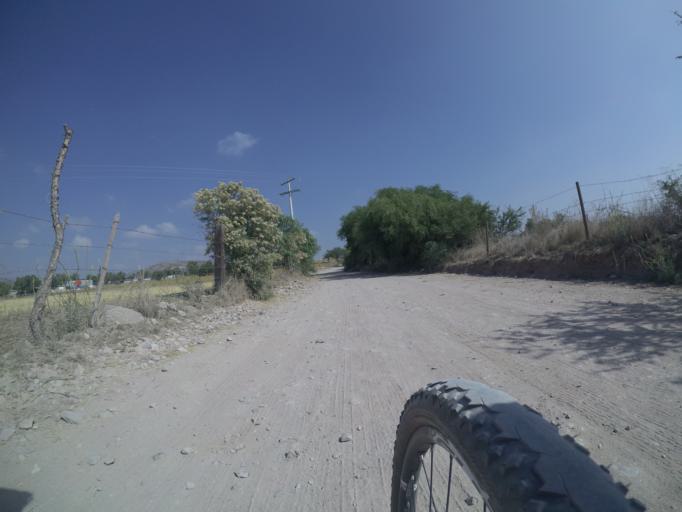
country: MX
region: Aguascalientes
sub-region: Jesus Maria
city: Paseos de las Haciendas [Fraccionamiento]
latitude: 21.9994
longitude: -102.3529
